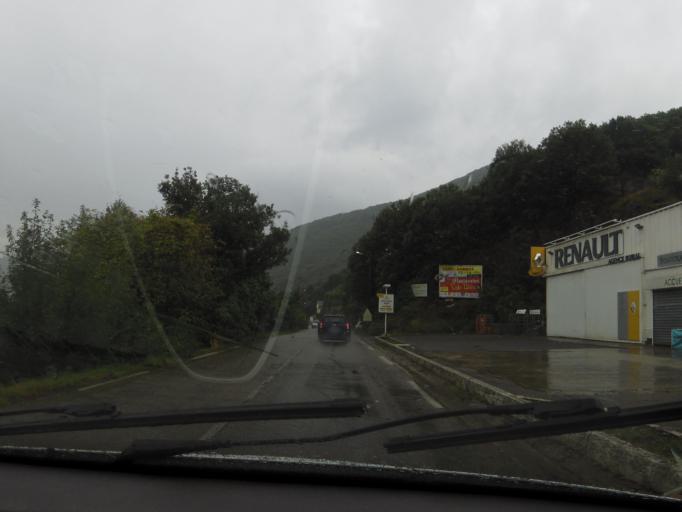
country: FR
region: Languedoc-Roussillon
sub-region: Departement du Gard
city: Les Salles-du-Gardon
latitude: 44.2025
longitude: 4.0332
